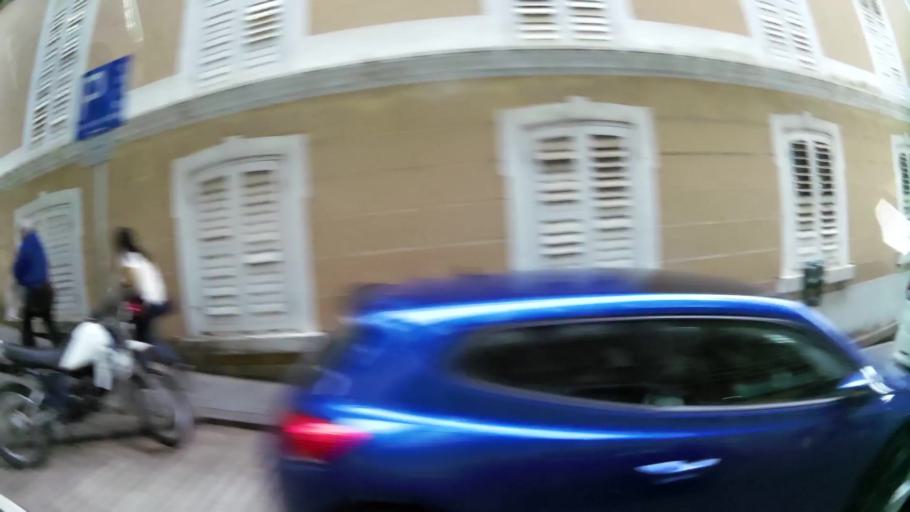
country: MO
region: Macau
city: Macau
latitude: 22.1953
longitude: 113.5433
